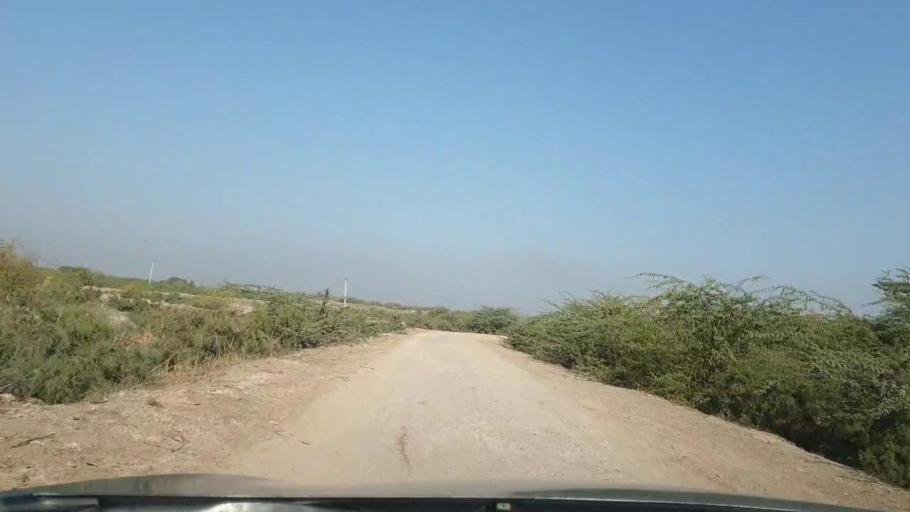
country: PK
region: Sindh
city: Berani
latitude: 25.6646
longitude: 68.9099
